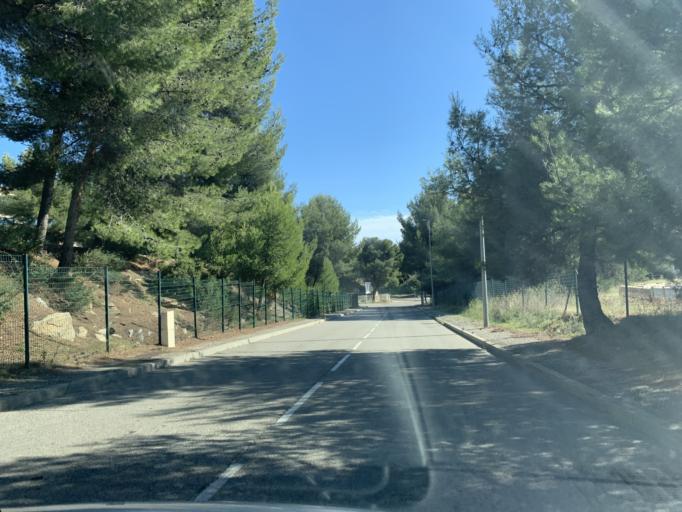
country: FR
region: Provence-Alpes-Cote d'Azur
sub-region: Departement des Bouches-du-Rhone
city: La Ciotat
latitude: 43.2062
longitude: 5.5998
